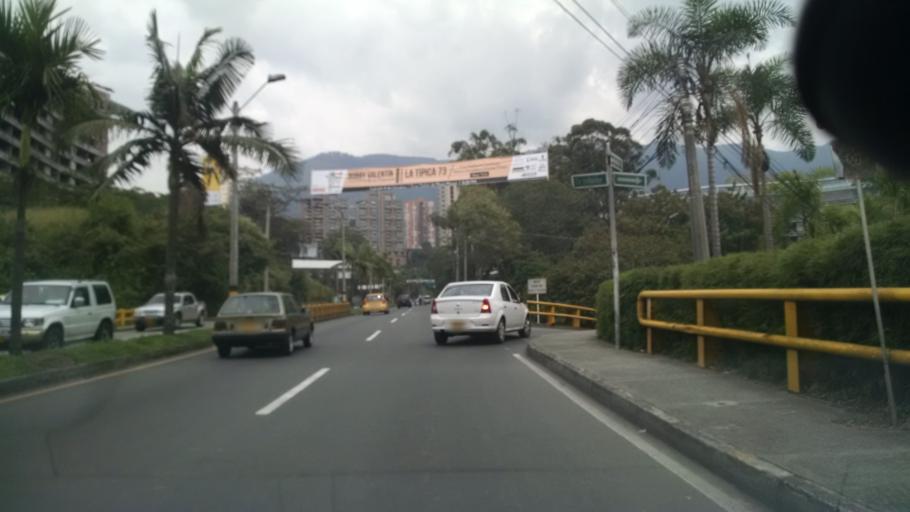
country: CO
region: Antioquia
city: Medellin
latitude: 6.2151
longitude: -75.5611
